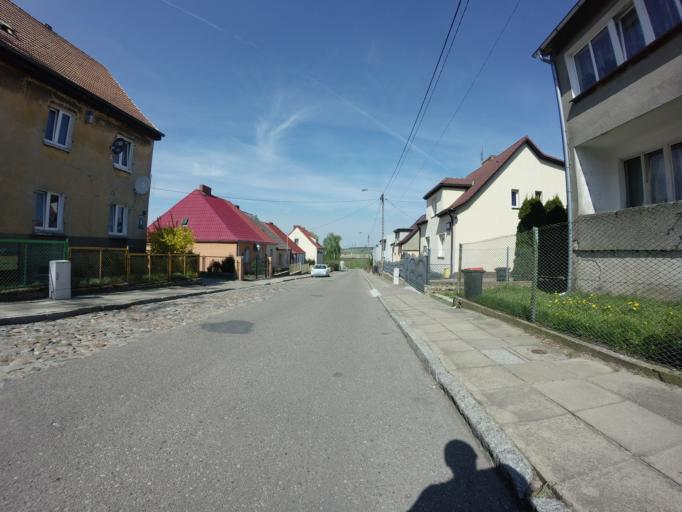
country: PL
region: West Pomeranian Voivodeship
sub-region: Powiat choszczenski
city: Choszczno
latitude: 53.1664
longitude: 15.3969
